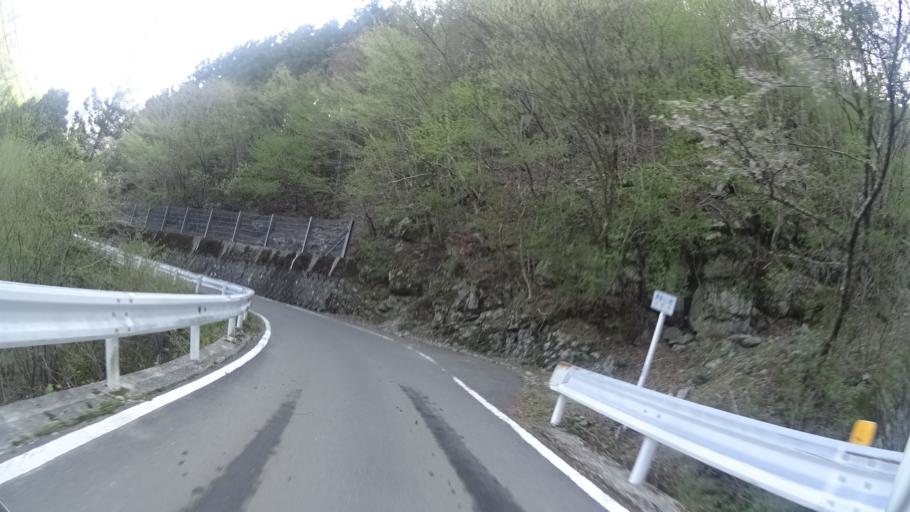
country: JP
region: Tokushima
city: Wakimachi
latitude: 33.8616
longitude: 134.0623
